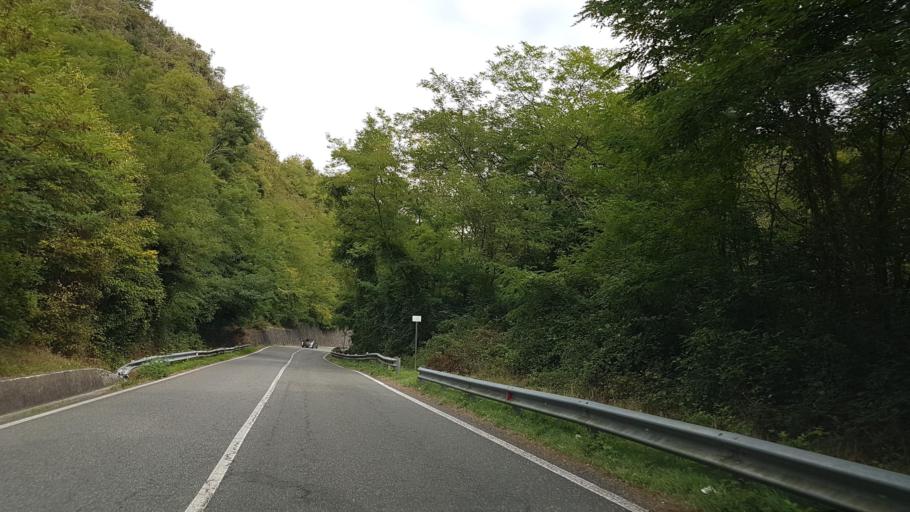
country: IT
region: Liguria
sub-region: Provincia di La Spezia
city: Carrodano
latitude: 44.2151
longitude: 9.6276
